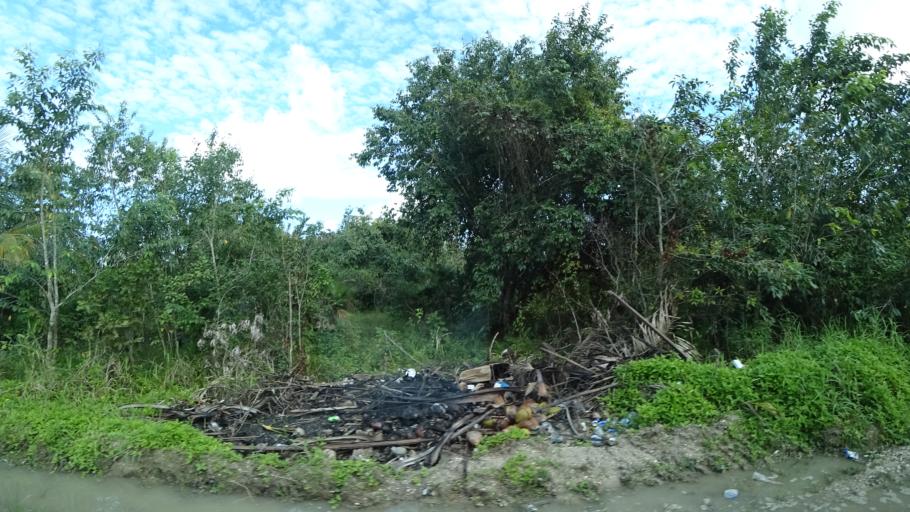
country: BZ
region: Belize
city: Belize City
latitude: 17.5662
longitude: -88.4086
